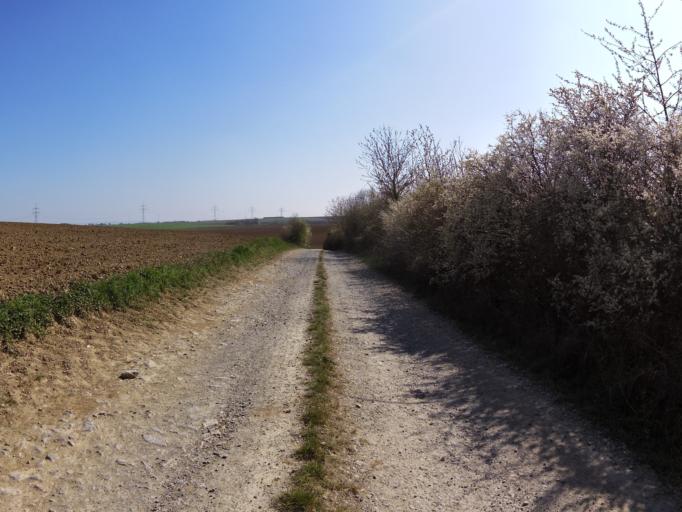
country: DE
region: Bavaria
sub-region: Regierungsbezirk Unterfranken
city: Oberpleichfeld
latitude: 49.8372
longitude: 10.0763
